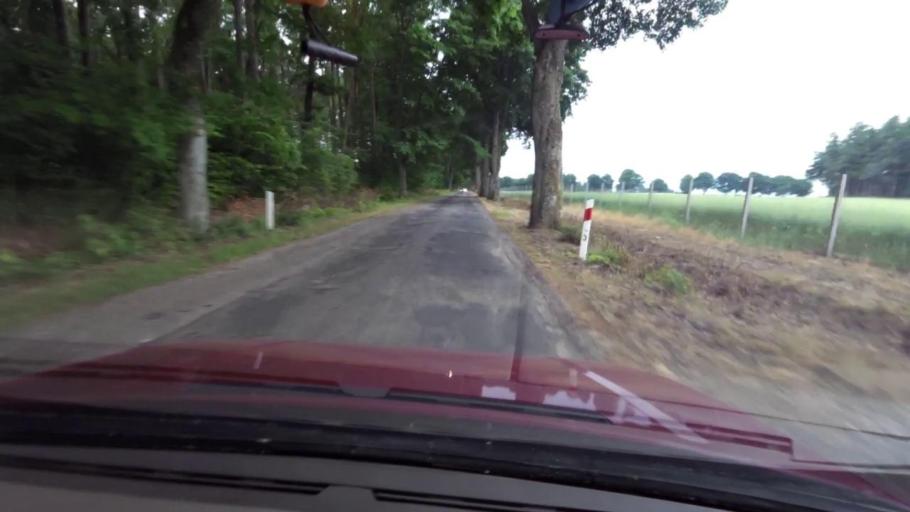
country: PL
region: Pomeranian Voivodeship
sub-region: Powiat slupski
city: Kepice
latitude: 54.2019
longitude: 16.8155
